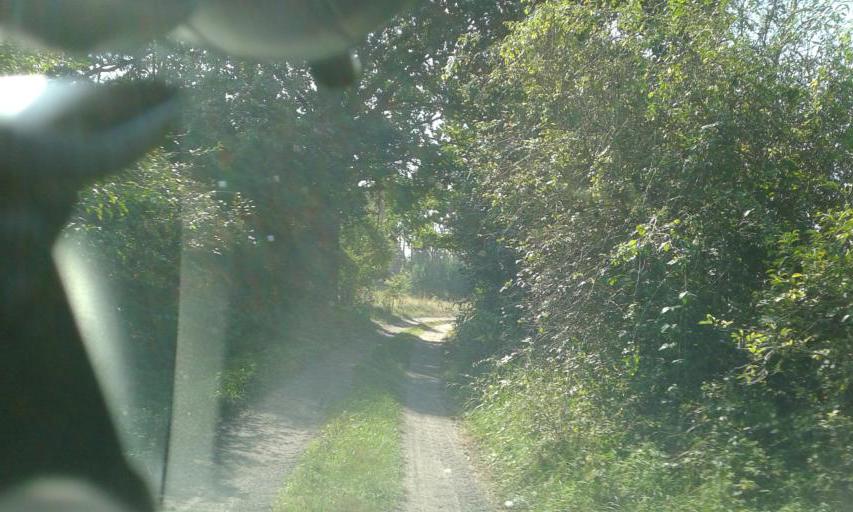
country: PL
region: West Pomeranian Voivodeship
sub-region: Powiat choszczenski
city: Krzecin
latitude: 53.0713
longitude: 15.5548
